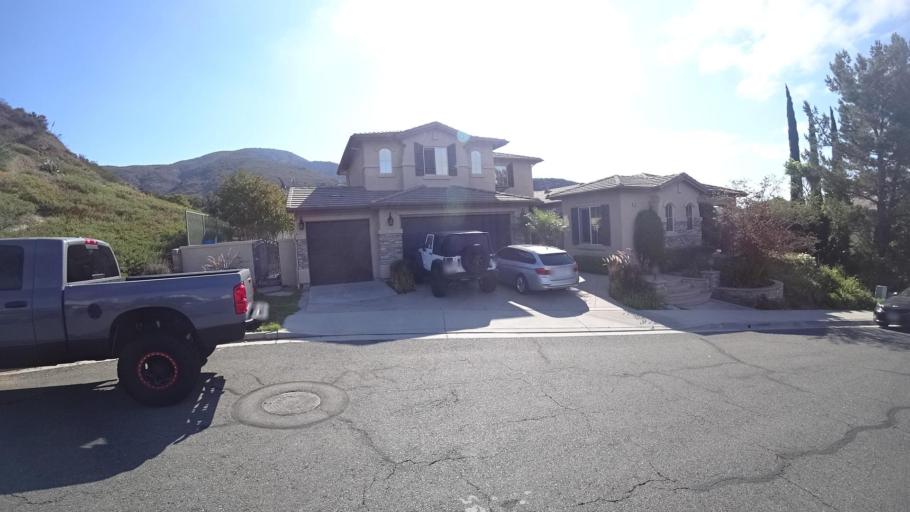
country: US
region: California
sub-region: Orange County
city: Portola Hills
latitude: 33.6934
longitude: -117.6189
